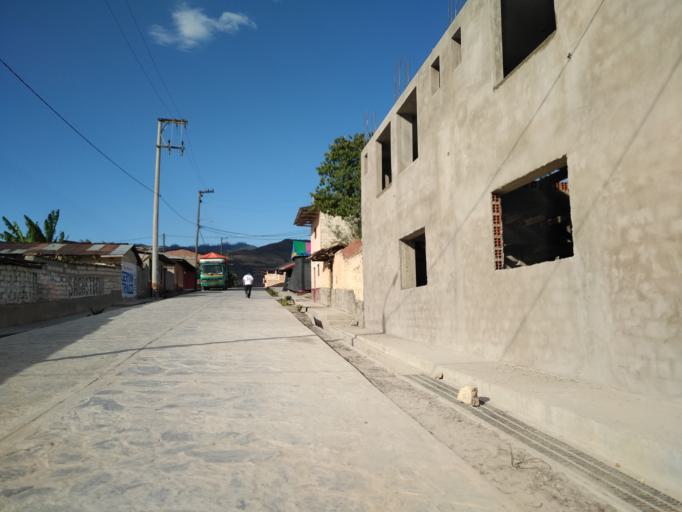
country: PE
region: Amazonas
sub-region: Provincia de Luya
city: Tingo
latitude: -6.3734
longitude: -77.9111
